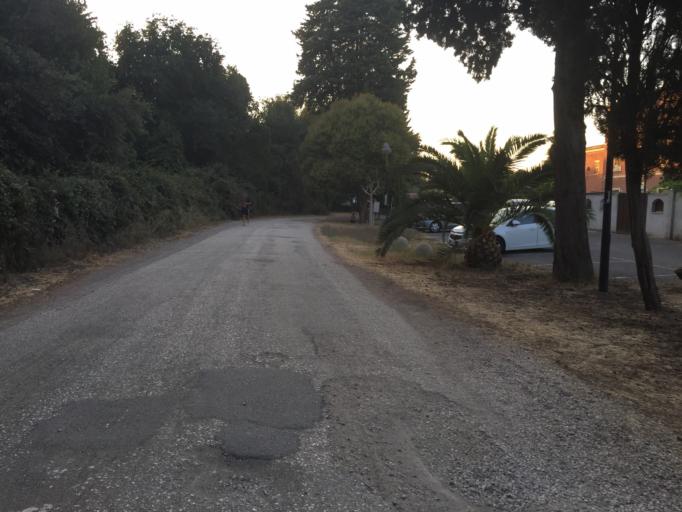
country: IT
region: Latium
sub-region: Citta metropolitana di Roma Capitale
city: Marina San Nicola
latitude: 41.9387
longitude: 12.1029
